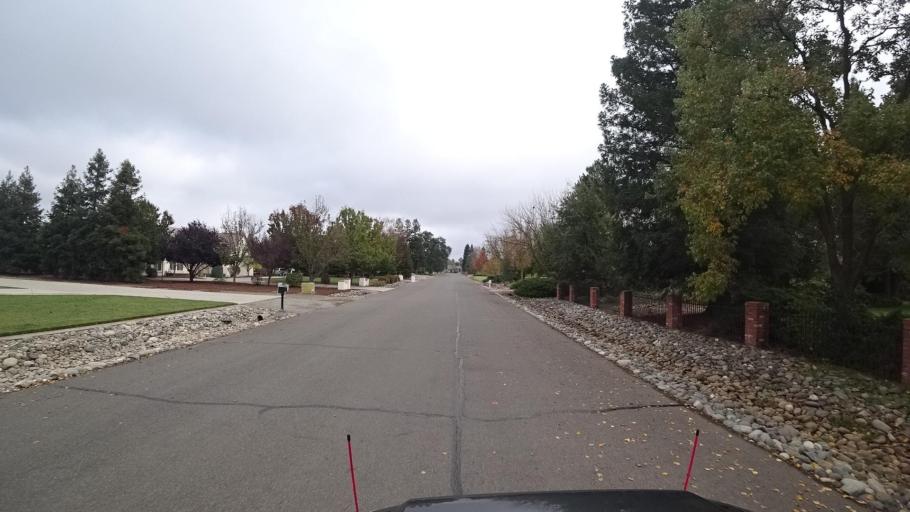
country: US
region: California
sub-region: Sacramento County
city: Vineyard
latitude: 38.4467
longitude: -121.3104
